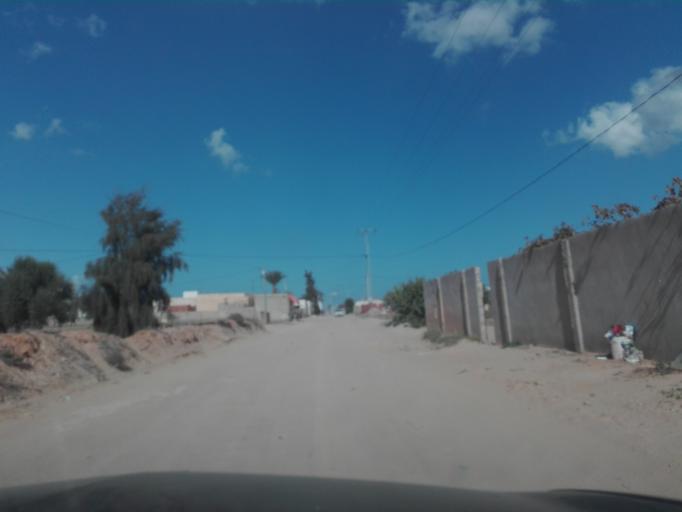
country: TN
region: Madanin
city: Bin Qirdan
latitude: 33.1552
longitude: 11.1937
